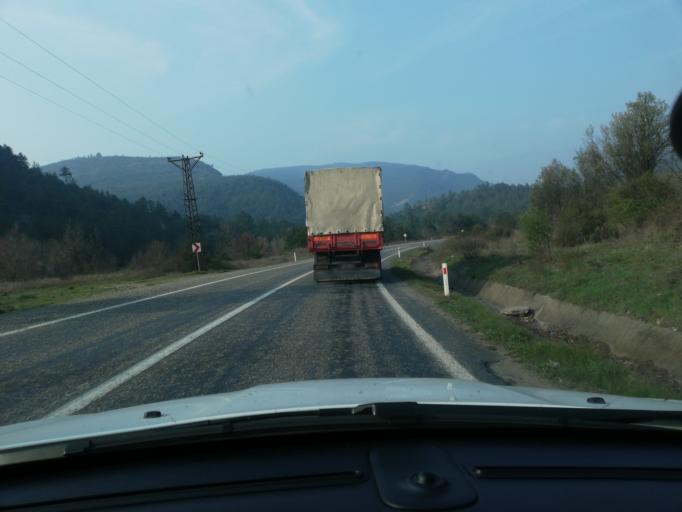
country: TR
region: Karabuk
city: Karabuk
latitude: 41.1669
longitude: 32.5783
